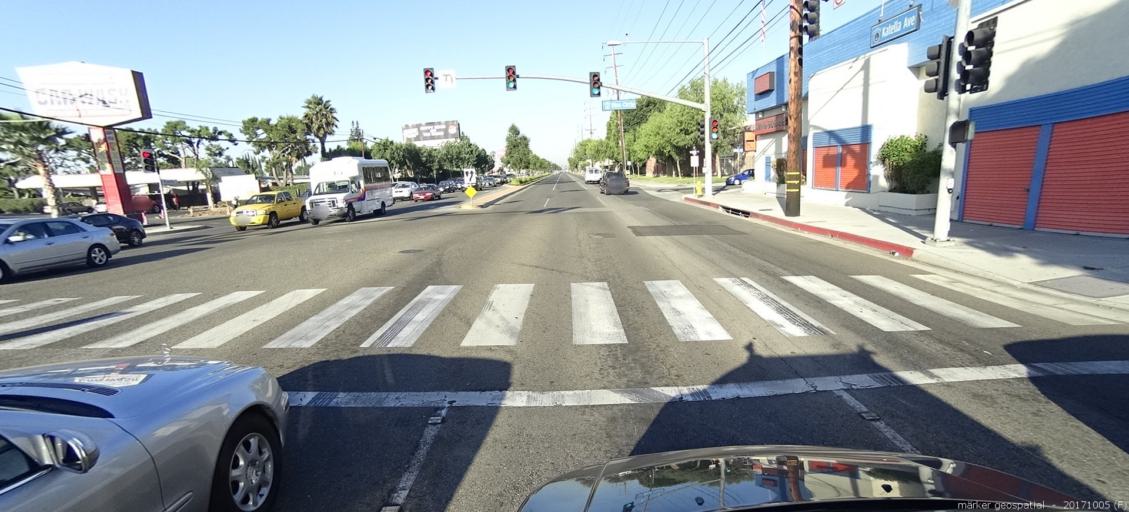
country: US
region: California
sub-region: Orange County
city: Garden Grove
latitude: 33.8032
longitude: -117.9441
